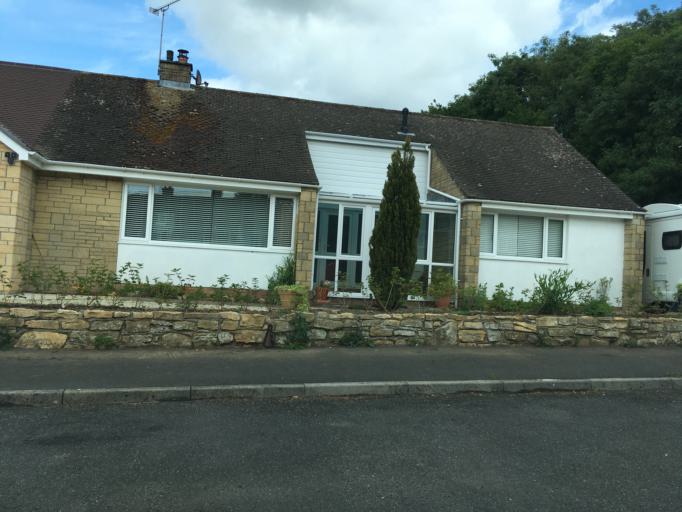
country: GB
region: England
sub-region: South Gloucestershire
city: Alveston
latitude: 51.5868
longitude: -2.5354
